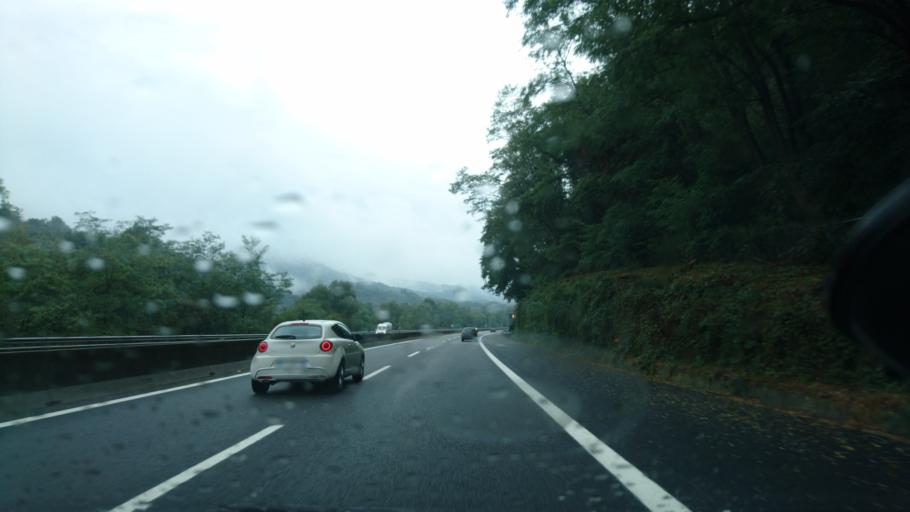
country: IT
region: Piedmont
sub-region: Provincia di Novara
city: Invorio
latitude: 45.7676
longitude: 8.4950
